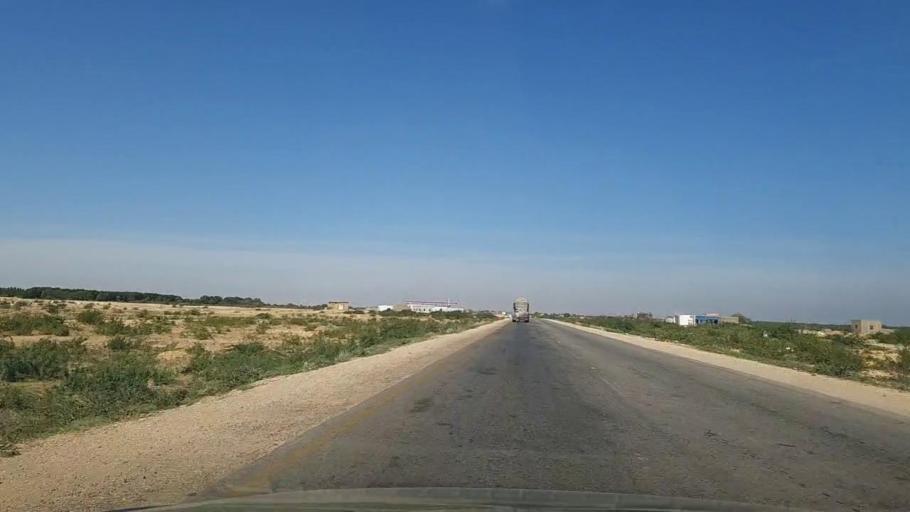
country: PK
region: Sindh
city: Kotri
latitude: 25.2125
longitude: 68.2376
